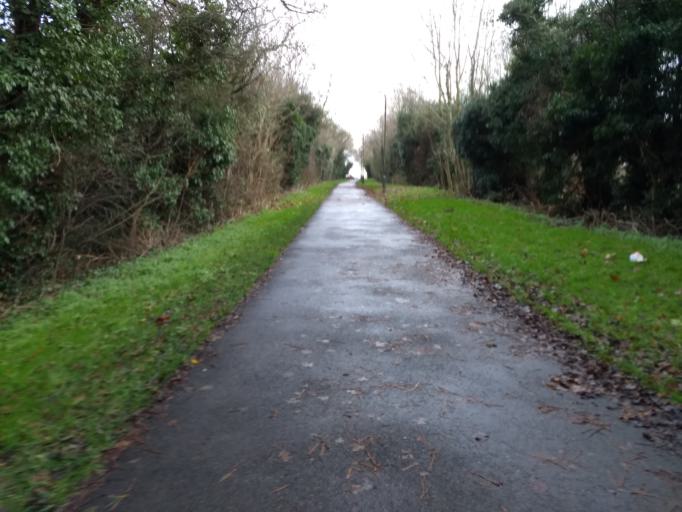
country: GB
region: England
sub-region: Buckinghamshire
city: Newton Longville
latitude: 51.9957
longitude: -0.7676
